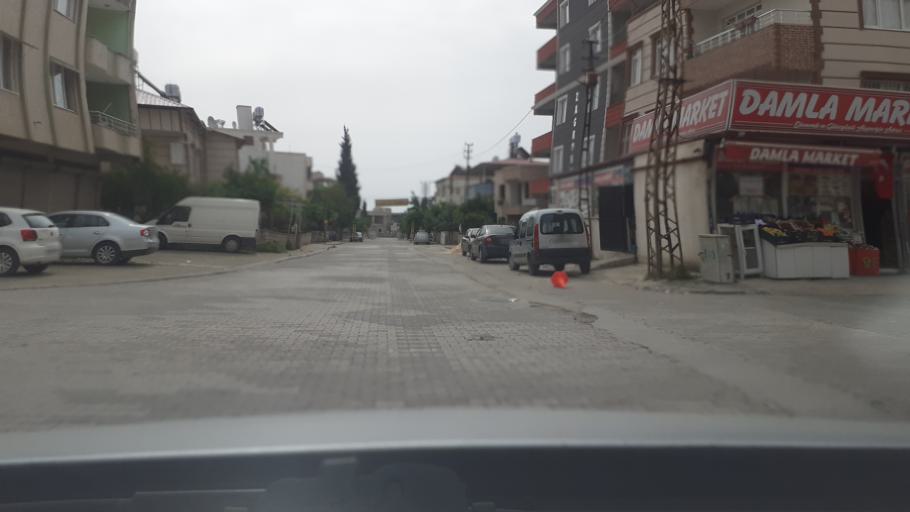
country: TR
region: Hatay
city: Kirikhan
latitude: 36.4949
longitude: 36.3645
